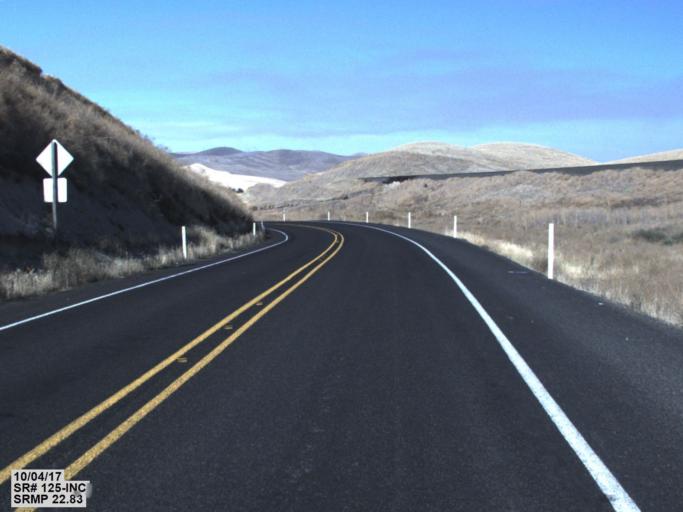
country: US
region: Washington
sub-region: Walla Walla County
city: Waitsburg
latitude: 46.2868
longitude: -118.3403
